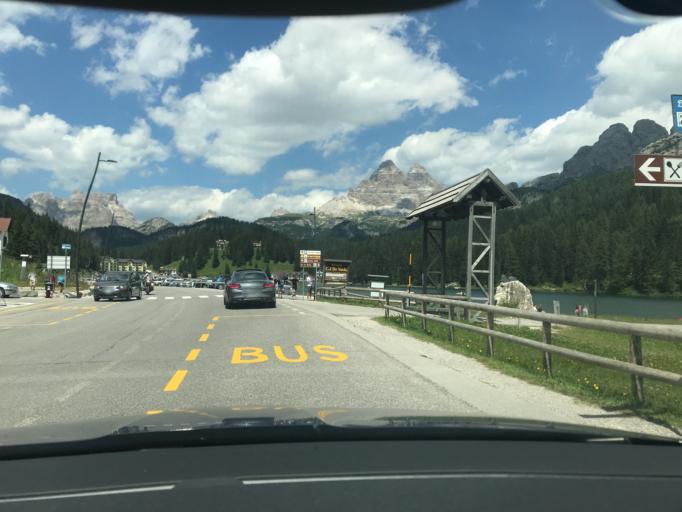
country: IT
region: Veneto
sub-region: Provincia di Belluno
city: Cortina d'Ampezzo
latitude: 46.5785
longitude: 12.2517
